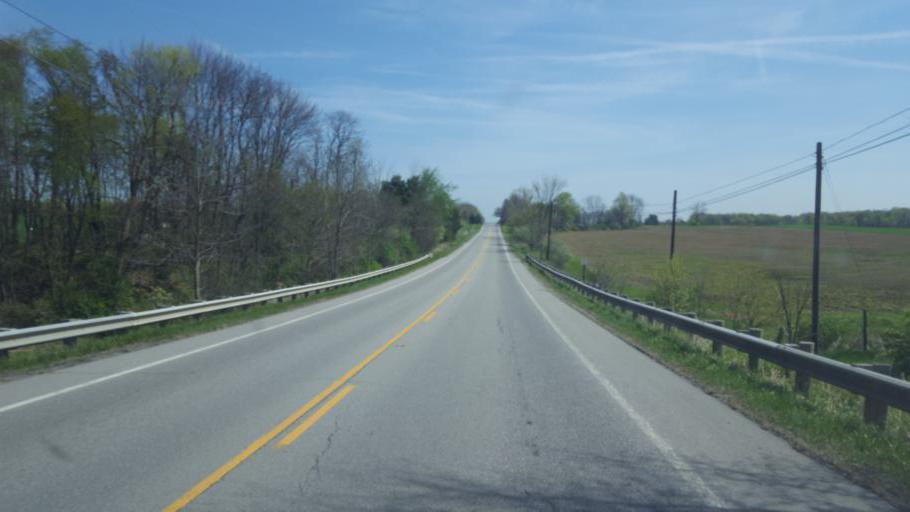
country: US
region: Ohio
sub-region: Wayne County
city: West Salem
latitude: 40.9980
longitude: -82.0723
